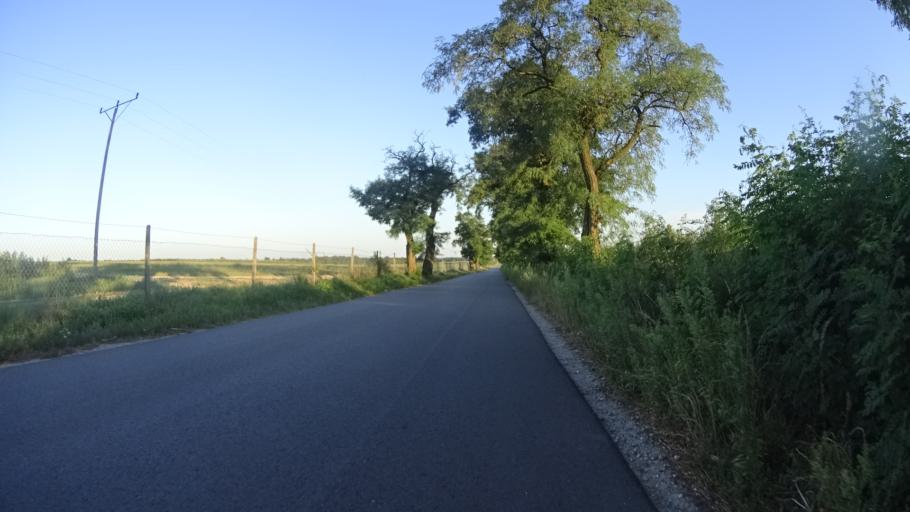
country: PL
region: Masovian Voivodeship
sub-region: Powiat grojecki
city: Goszczyn
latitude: 51.6862
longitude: 20.8215
